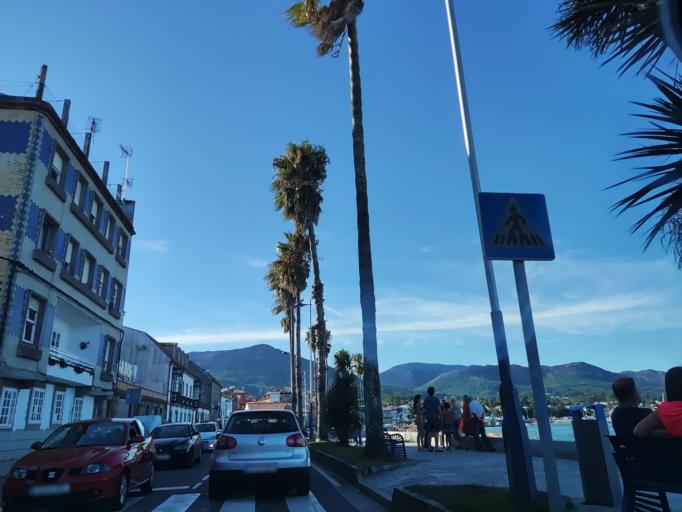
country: ES
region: Galicia
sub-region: Provincia da Coruna
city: Boiro
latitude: 42.6008
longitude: -8.9355
